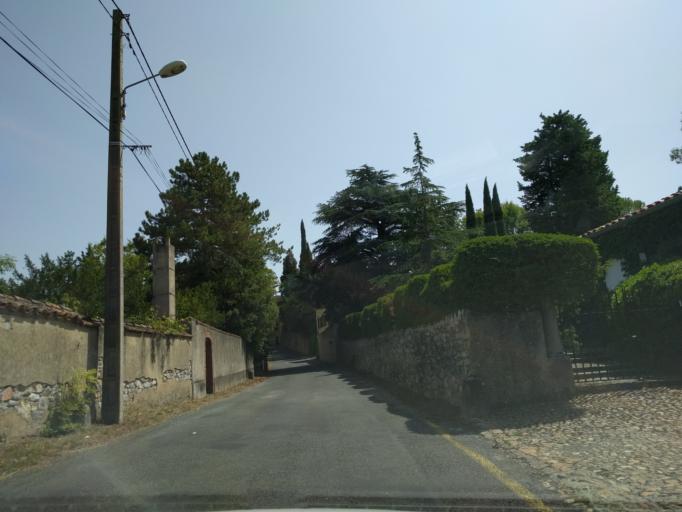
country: FR
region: Midi-Pyrenees
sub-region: Departement du Tarn
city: Castres
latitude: 43.5997
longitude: 2.2480
